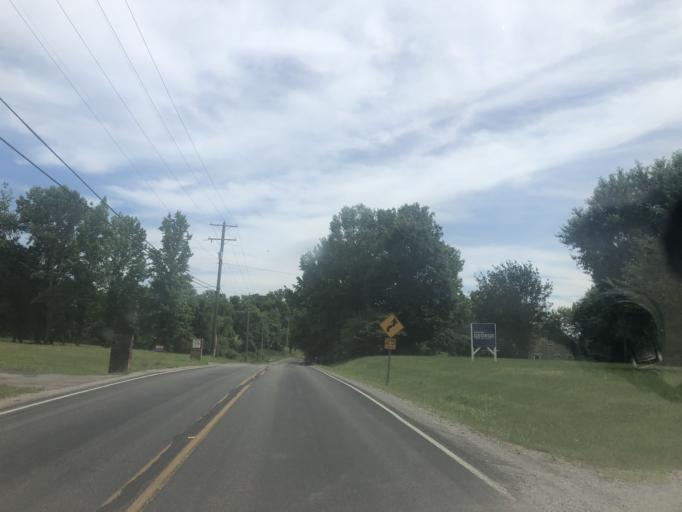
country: US
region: Tennessee
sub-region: Davidson County
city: Lakewood
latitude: 36.2243
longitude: -86.6675
